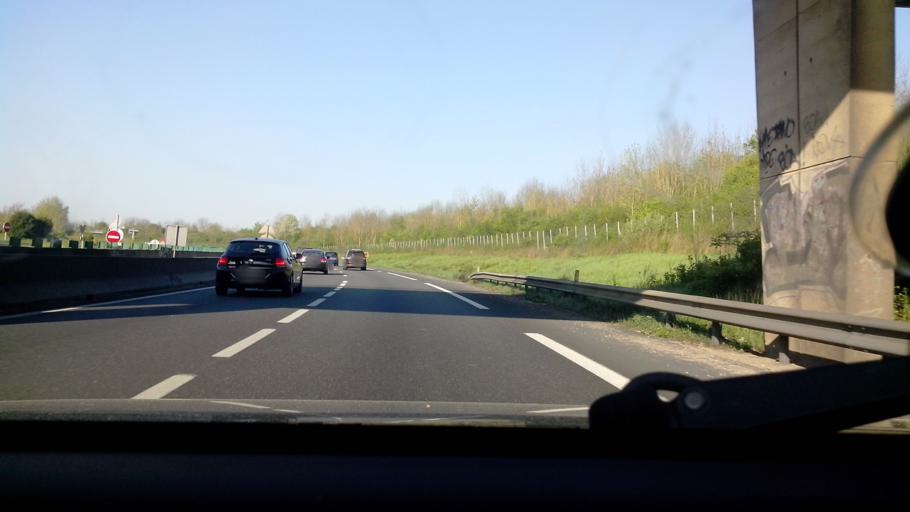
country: FR
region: Ile-de-France
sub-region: Departement de Seine-et-Marne
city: Servon
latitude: 48.7281
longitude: 2.6032
